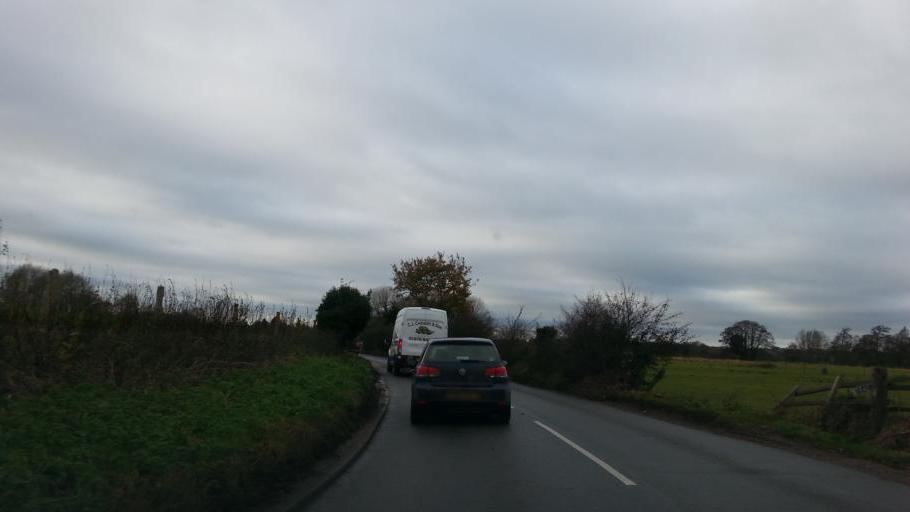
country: GB
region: England
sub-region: Norfolk
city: Diss
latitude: 52.3559
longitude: 1.1982
